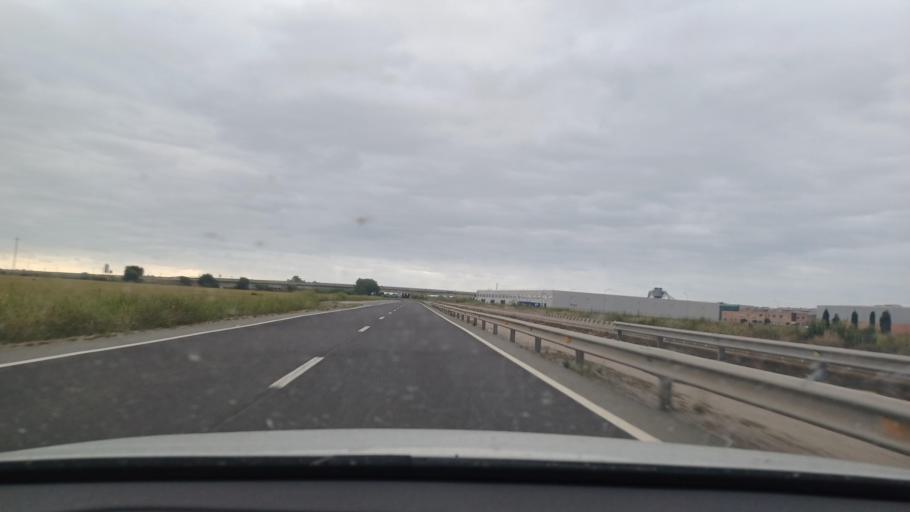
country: ES
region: Catalonia
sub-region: Provincia de Tarragona
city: Amposta
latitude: 40.7170
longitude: 0.5888
